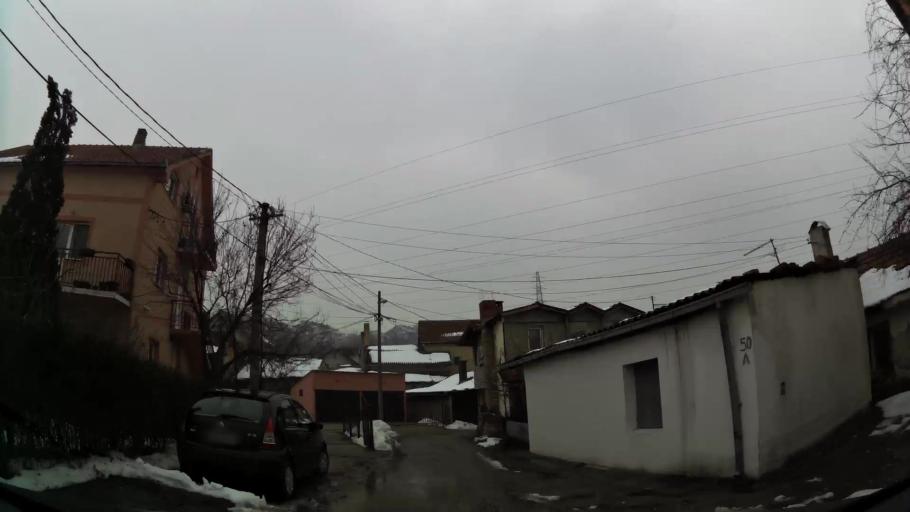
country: RS
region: Central Serbia
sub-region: Belgrade
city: Zvezdara
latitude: 44.7766
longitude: 20.5082
